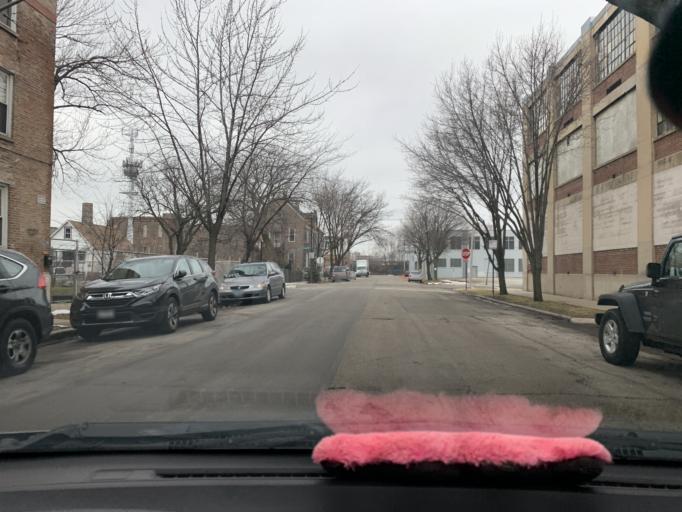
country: US
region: Illinois
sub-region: Cook County
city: Chicago
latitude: 41.8543
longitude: -87.6906
